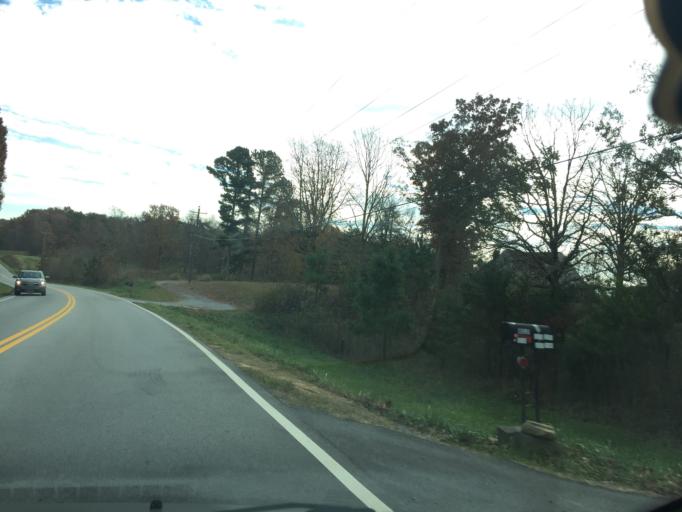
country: US
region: Georgia
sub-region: Dade County
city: Trenton
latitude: 34.8192
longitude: -85.4969
